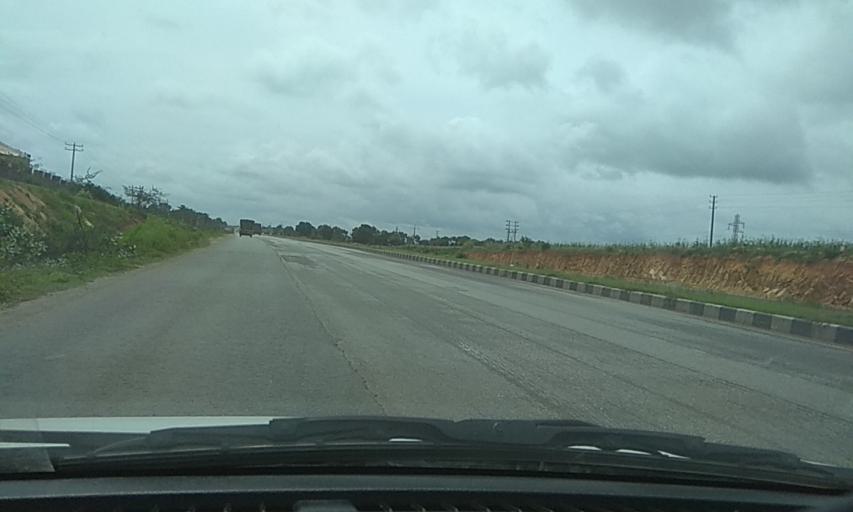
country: IN
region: Karnataka
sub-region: Davanagere
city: Mayakonda
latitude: 14.3361
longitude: 76.2135
